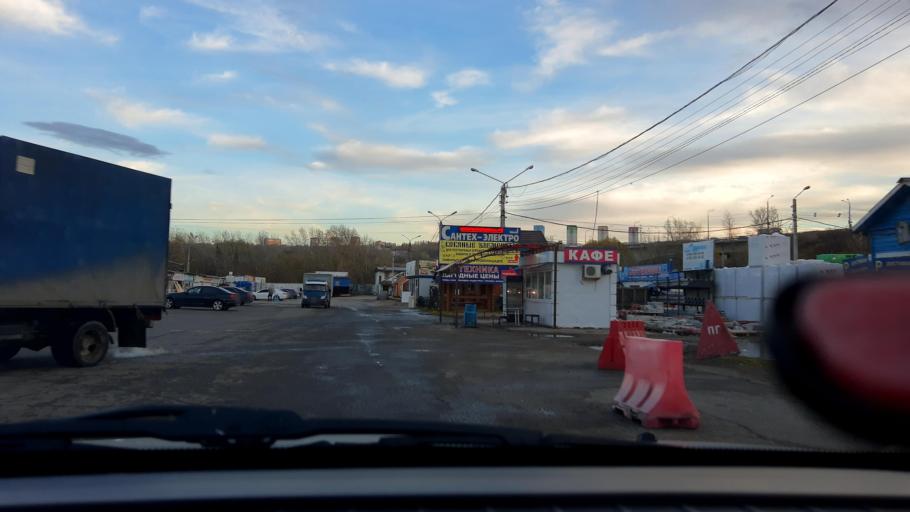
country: RU
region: Nizjnij Novgorod
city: Nizhniy Novgorod
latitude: 56.2555
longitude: 43.9404
